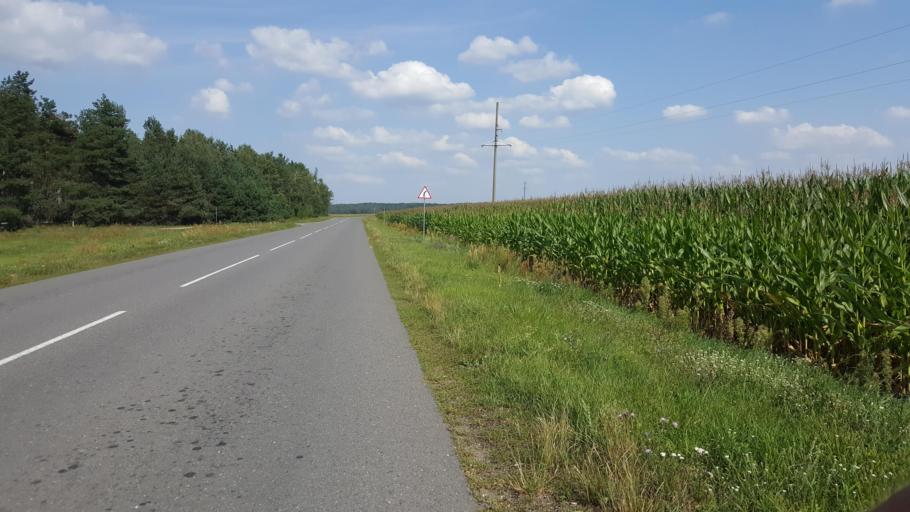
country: BY
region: Brest
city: Kamyanyuki
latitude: 52.5018
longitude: 23.6126
